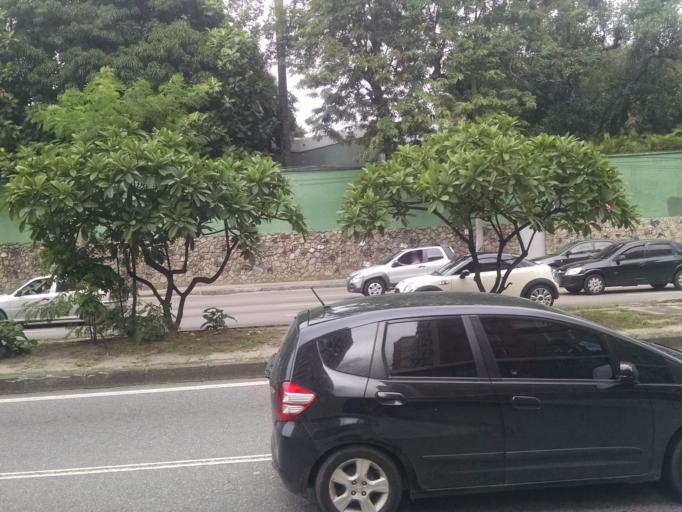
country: BR
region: Rio de Janeiro
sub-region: Rio De Janeiro
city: Rio de Janeiro
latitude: -22.9785
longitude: -43.2272
